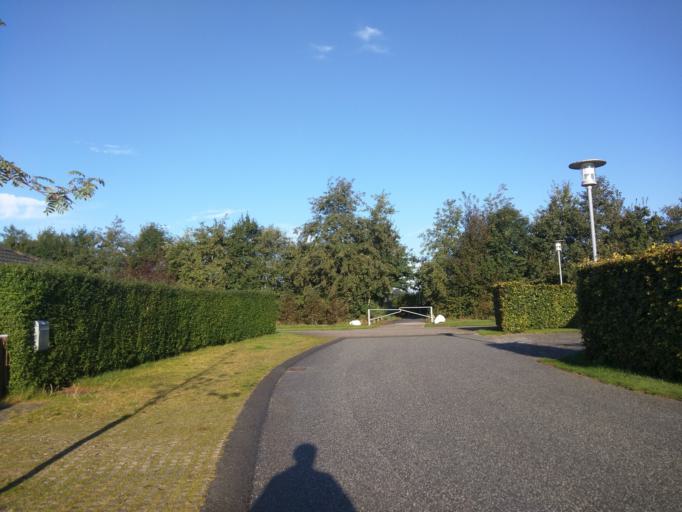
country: DK
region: Central Jutland
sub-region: Viborg Kommune
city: Viborg
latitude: 56.4365
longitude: 9.3725
